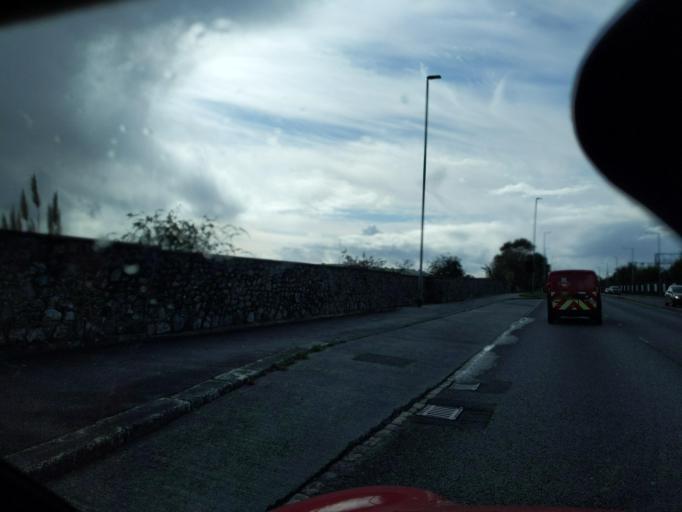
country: GB
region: England
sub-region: Plymouth
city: Plymstock
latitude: 50.3819
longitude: -4.1025
